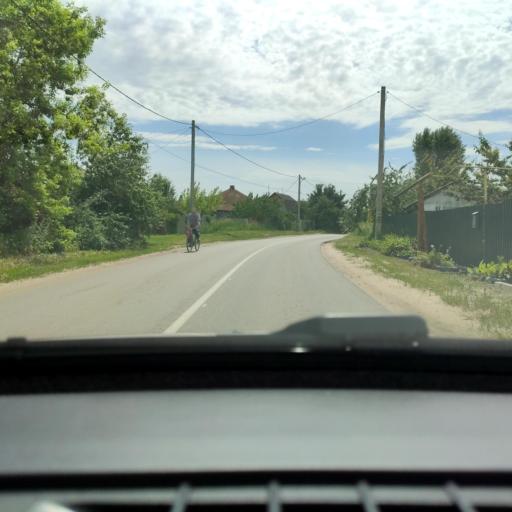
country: RU
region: Voronezj
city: Shilovo
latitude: 51.5240
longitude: 39.1493
